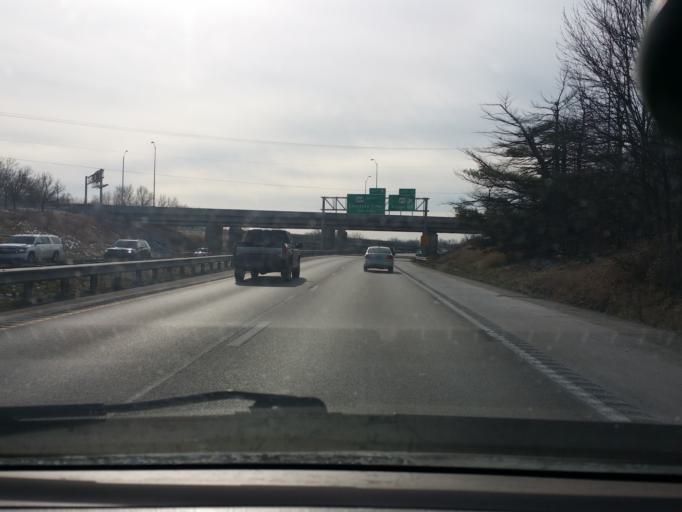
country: US
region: Missouri
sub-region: Clay County
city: Claycomo
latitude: 39.1896
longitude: -94.5155
